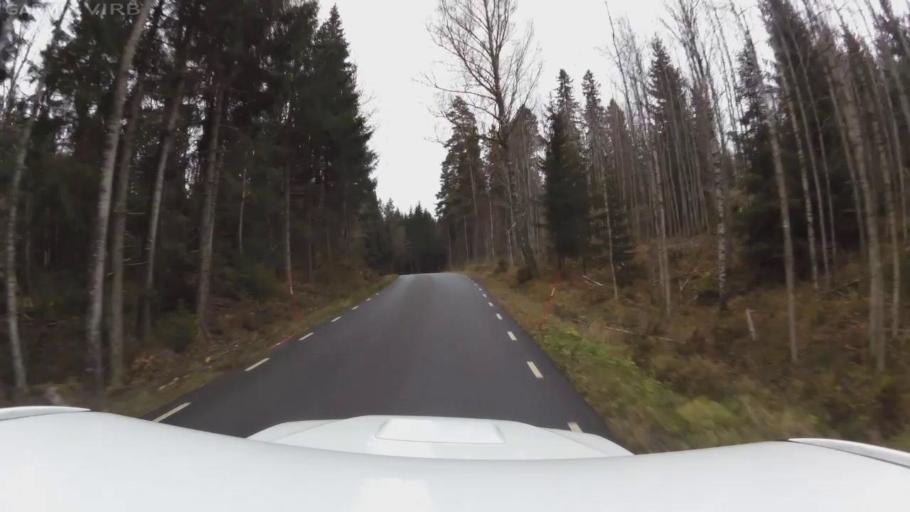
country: SE
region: OEstergoetland
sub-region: Mjolby Kommun
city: Mantorp
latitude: 58.1740
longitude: 15.3975
